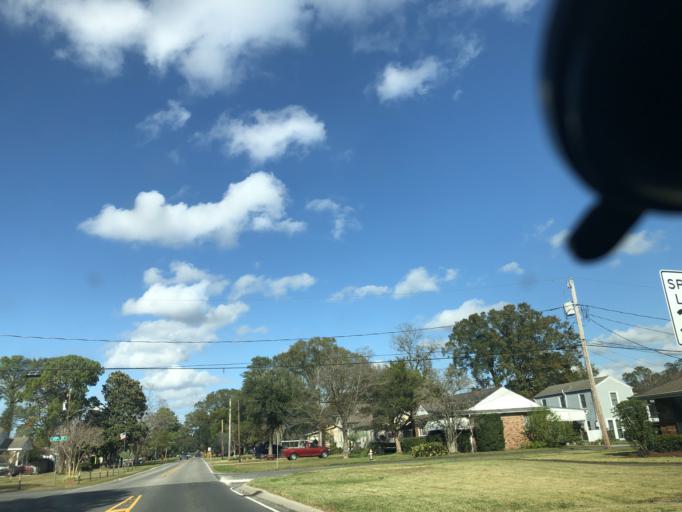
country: US
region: Louisiana
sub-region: Jefferson Parish
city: Metairie Terrace
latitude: 29.9826
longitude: -90.1602
